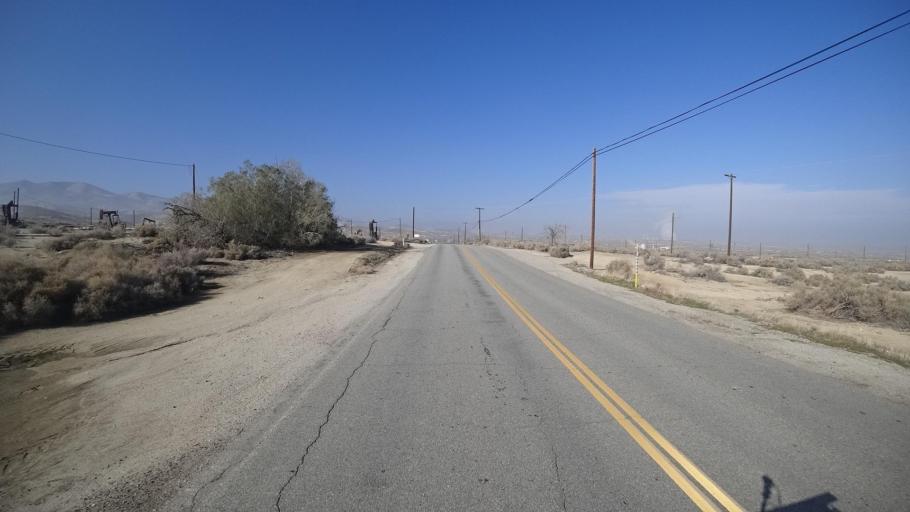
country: US
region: California
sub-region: Kern County
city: Taft Heights
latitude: 35.1873
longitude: -119.5652
